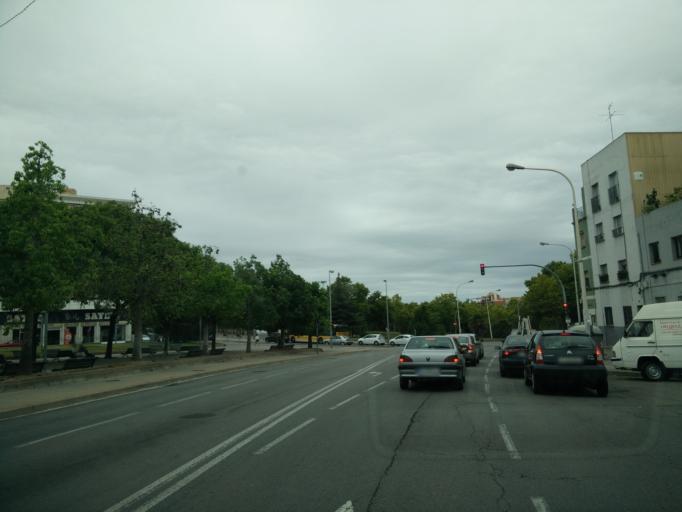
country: ES
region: Catalonia
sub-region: Provincia de Barcelona
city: Llefia
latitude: 41.4536
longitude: 2.2271
